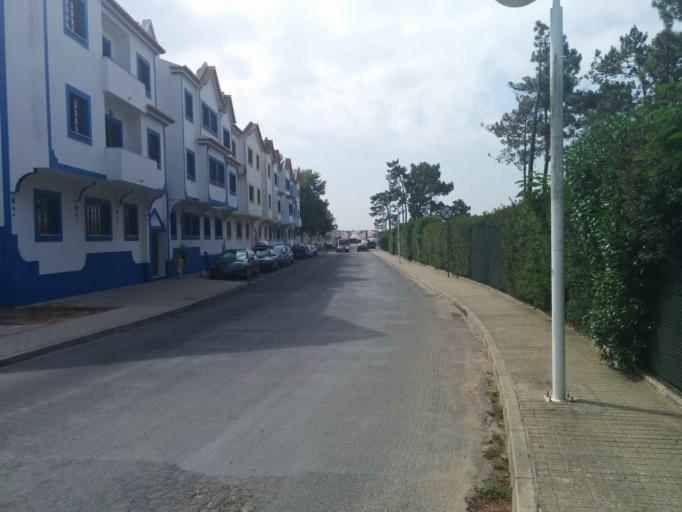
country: PT
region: Beja
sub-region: Odemira
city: Vila Nova de Milfontes
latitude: 37.7305
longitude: -8.7830
